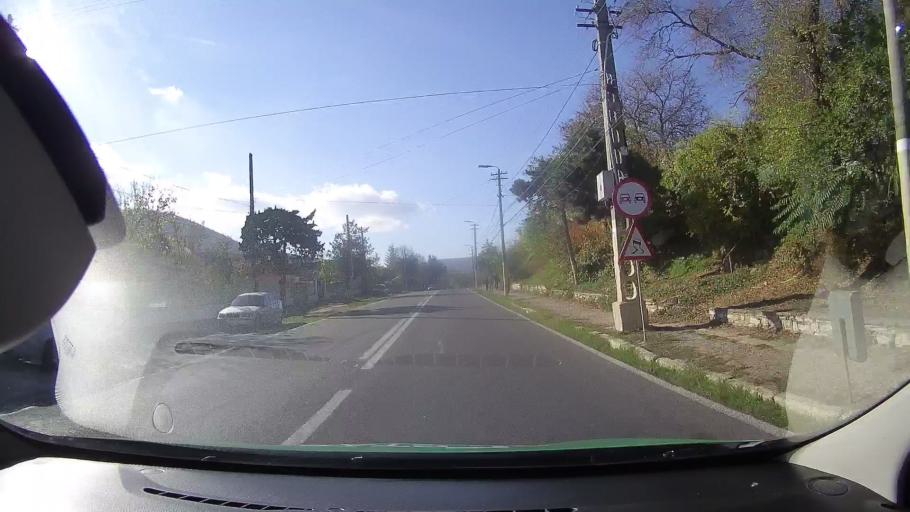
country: RO
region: Tulcea
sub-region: Oras Babadag
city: Babadag
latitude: 44.8858
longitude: 28.7030
